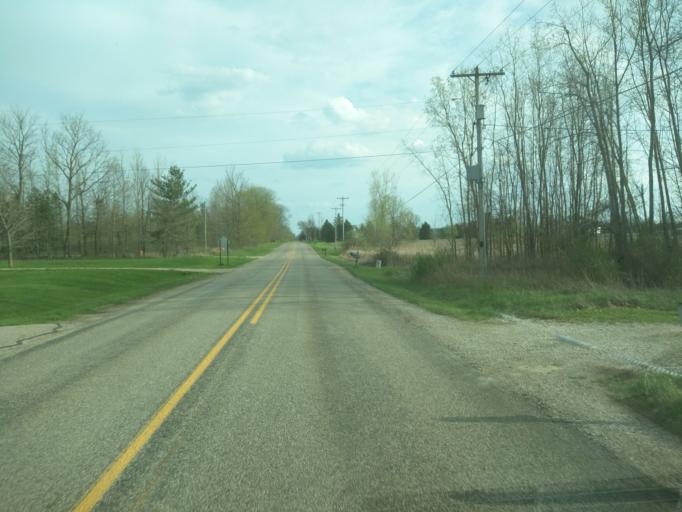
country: US
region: Michigan
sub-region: Eaton County
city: Dimondale
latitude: 42.6332
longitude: -84.6420
